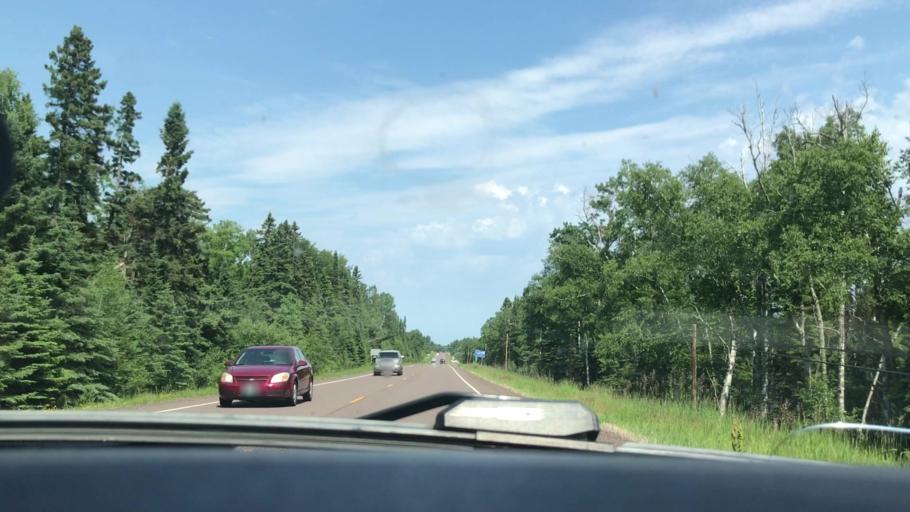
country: US
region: Minnesota
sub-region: Cook County
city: Grand Marais
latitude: 47.6431
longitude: -90.6914
